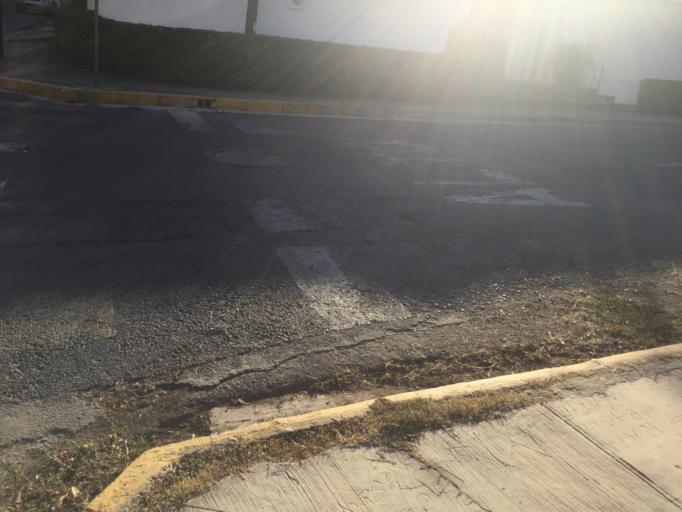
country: MX
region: Nuevo Leon
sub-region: San Pedro Garza Garcia
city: San Pedro Garza Garcia
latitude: 25.6577
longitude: -100.4027
